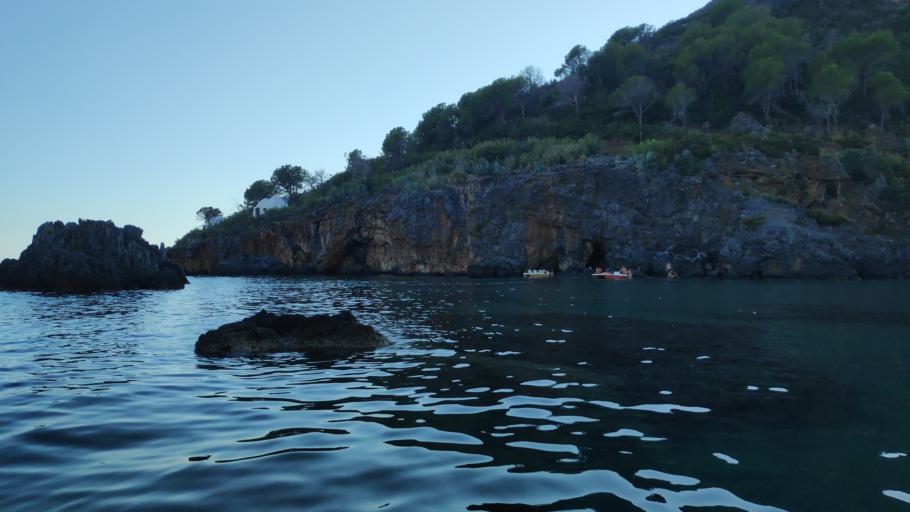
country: IT
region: Calabria
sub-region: Provincia di Cosenza
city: Praia a Mare
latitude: 39.8735
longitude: 15.7814
